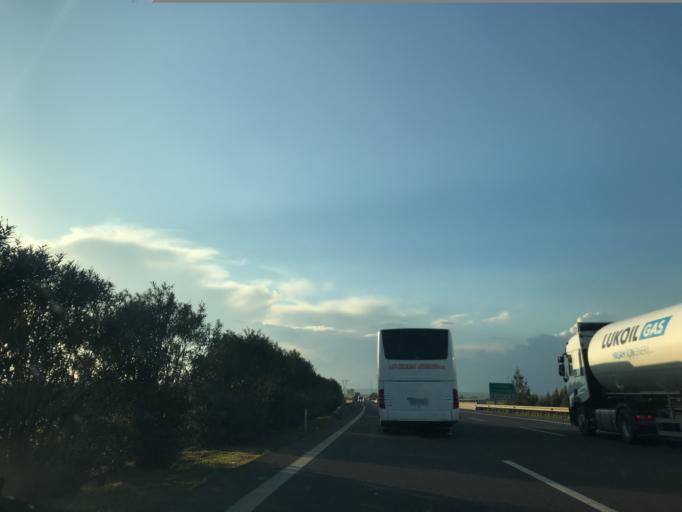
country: TR
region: Adana
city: Ceyhan
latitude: 37.0024
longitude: 35.7258
